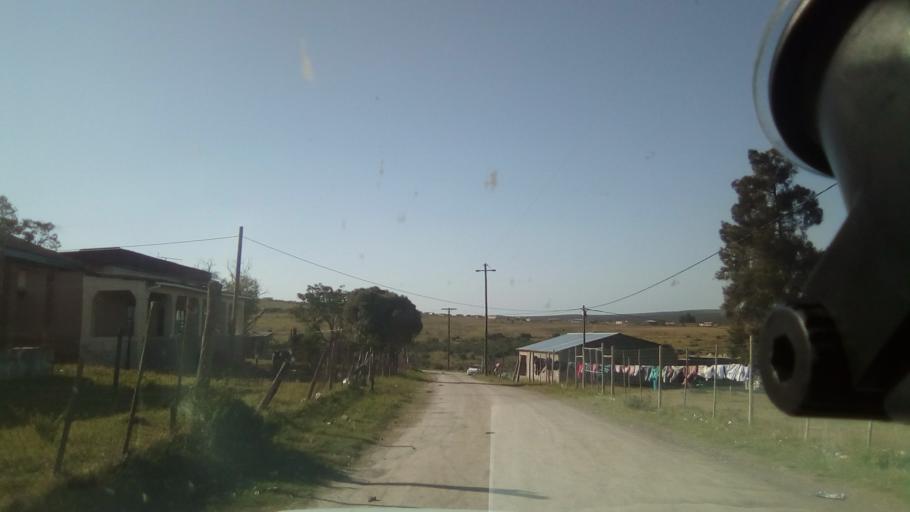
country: ZA
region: Eastern Cape
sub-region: Buffalo City Metropolitan Municipality
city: Bhisho
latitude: -32.8113
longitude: 27.3576
